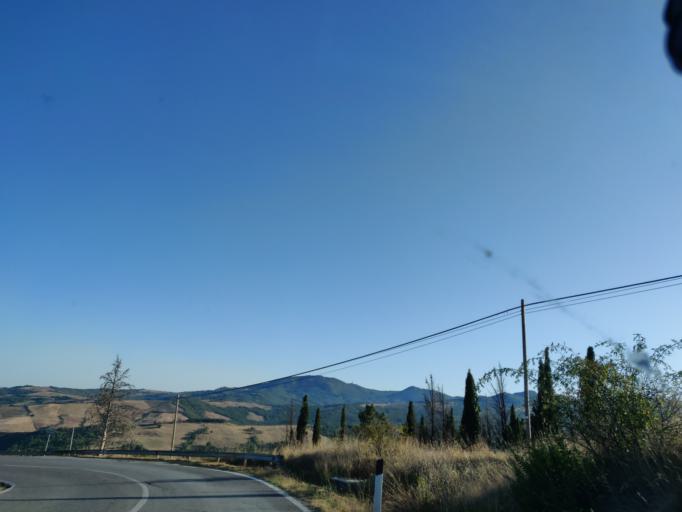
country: IT
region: Tuscany
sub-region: Provincia di Siena
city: Piancastagnaio
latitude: 42.8390
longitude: 11.7076
